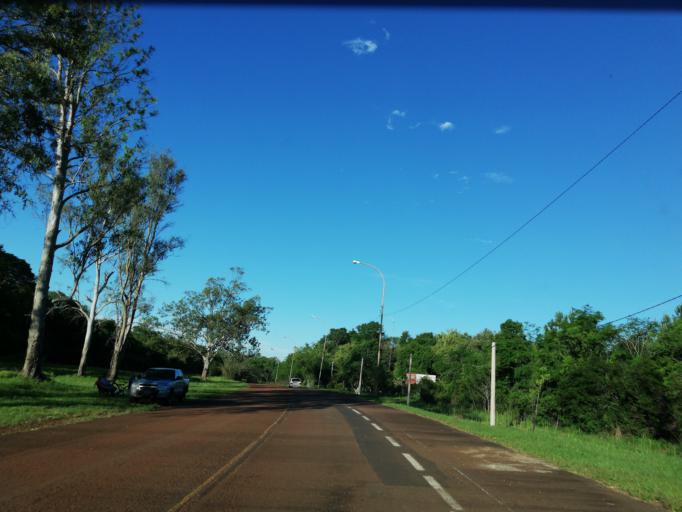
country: AR
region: Misiones
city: Garupa
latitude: -27.4601
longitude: -55.8172
